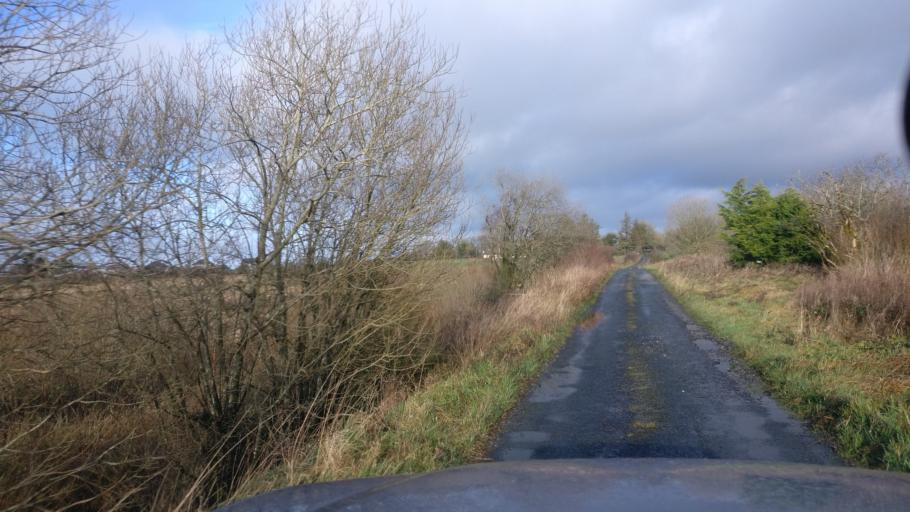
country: IE
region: Connaught
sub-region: County Galway
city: Loughrea
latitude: 53.2383
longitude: -8.5335
